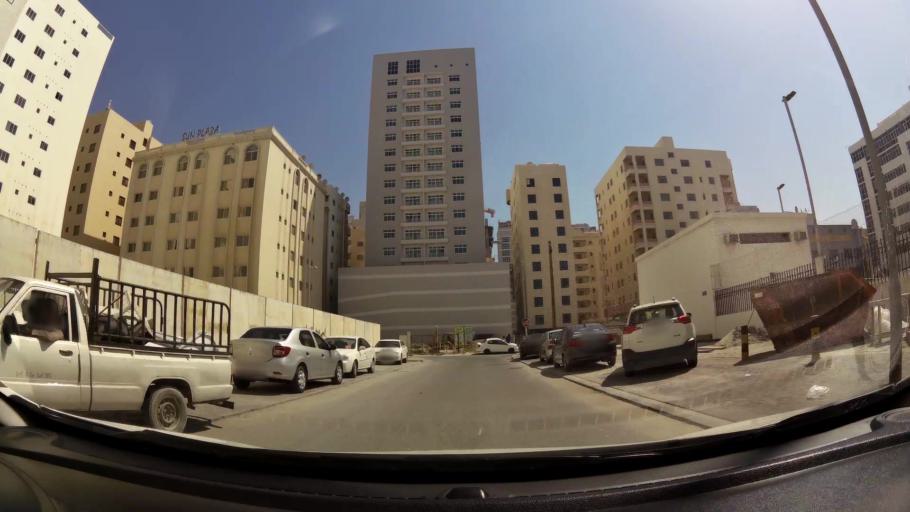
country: BH
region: Manama
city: Manama
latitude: 26.2121
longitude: 50.6066
